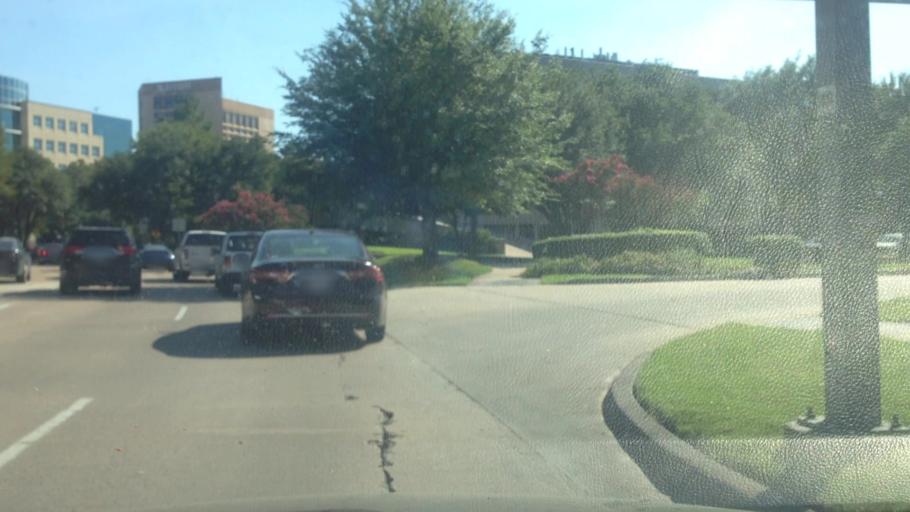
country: US
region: Texas
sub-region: Dallas County
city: Coppell
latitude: 32.9254
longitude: -97.0173
